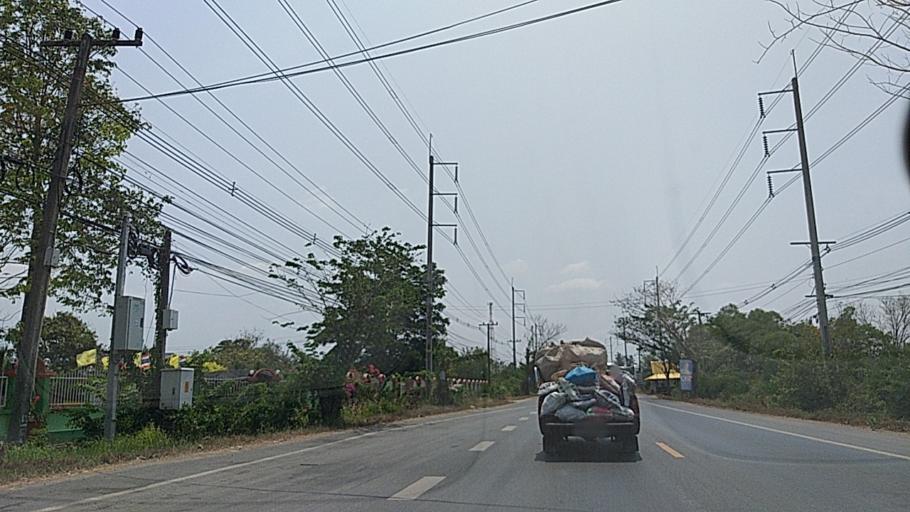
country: TH
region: Chachoengsao
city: Bang Nam Priao
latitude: 13.8006
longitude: 101.0532
